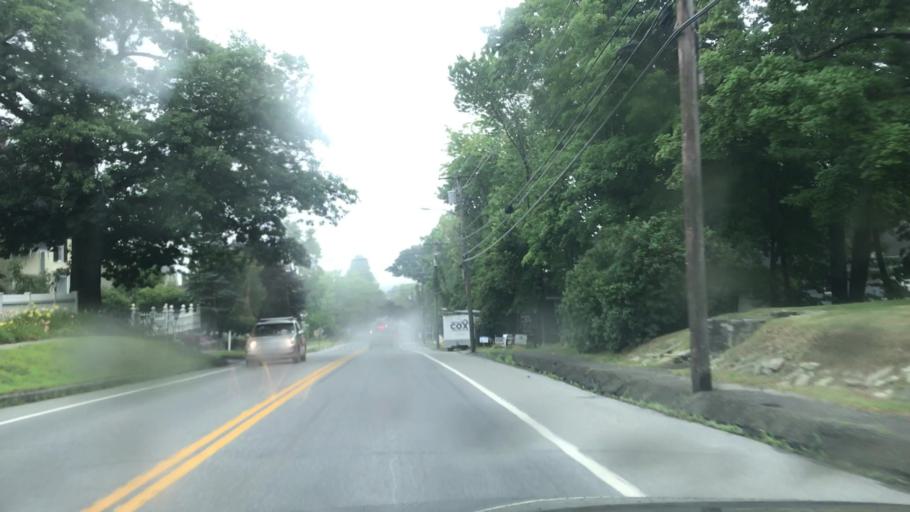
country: US
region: Maine
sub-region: Knox County
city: Camden
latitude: 44.2062
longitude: -69.0695
